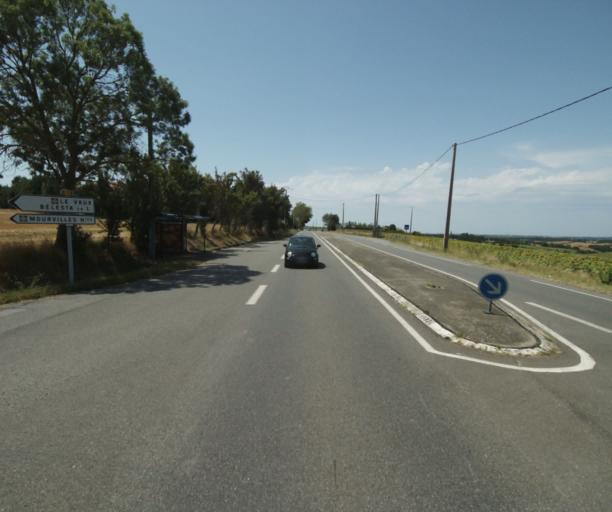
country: FR
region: Midi-Pyrenees
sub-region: Departement de la Haute-Garonne
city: Saint-Felix-Lauragais
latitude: 43.4613
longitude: 1.8352
